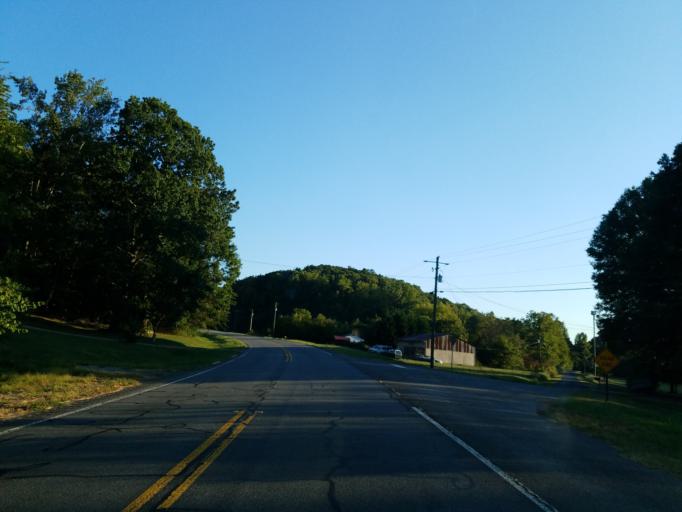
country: US
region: Georgia
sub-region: Bartow County
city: Rydal
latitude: 34.3989
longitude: -84.7091
